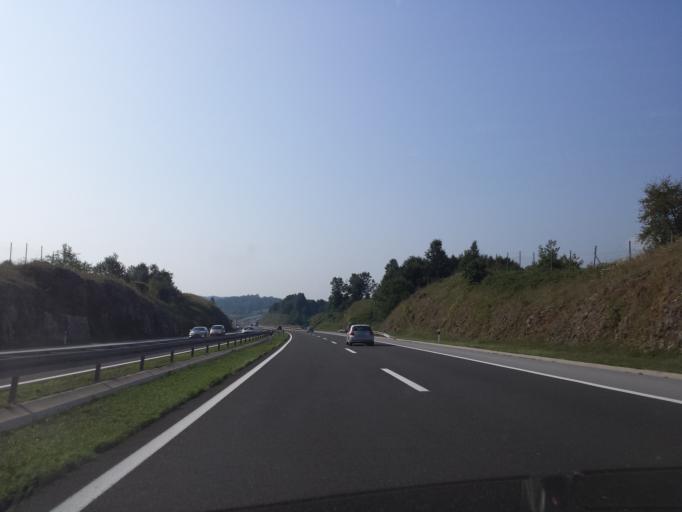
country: HR
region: Karlovacka
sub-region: Grad Ogulin
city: Ogulin
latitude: 45.3322
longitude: 15.2765
